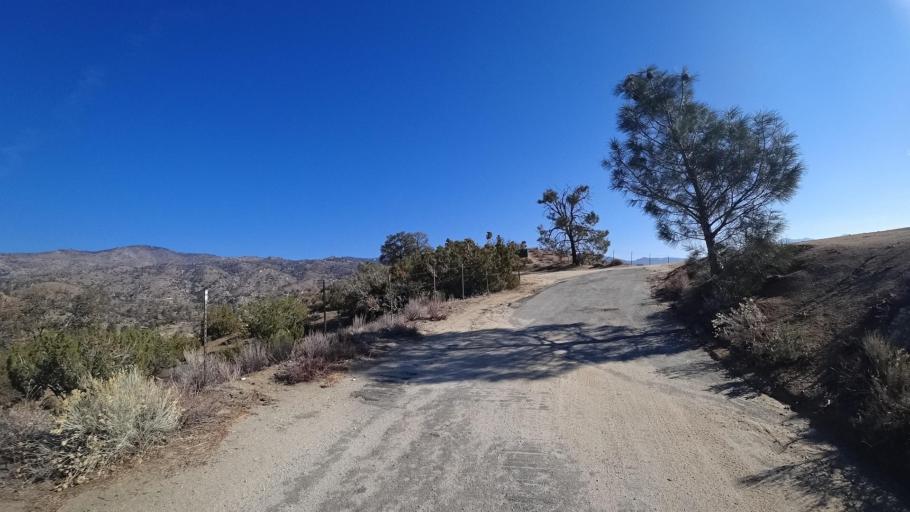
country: US
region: California
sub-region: Kern County
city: Bodfish
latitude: 35.3830
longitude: -118.4112
